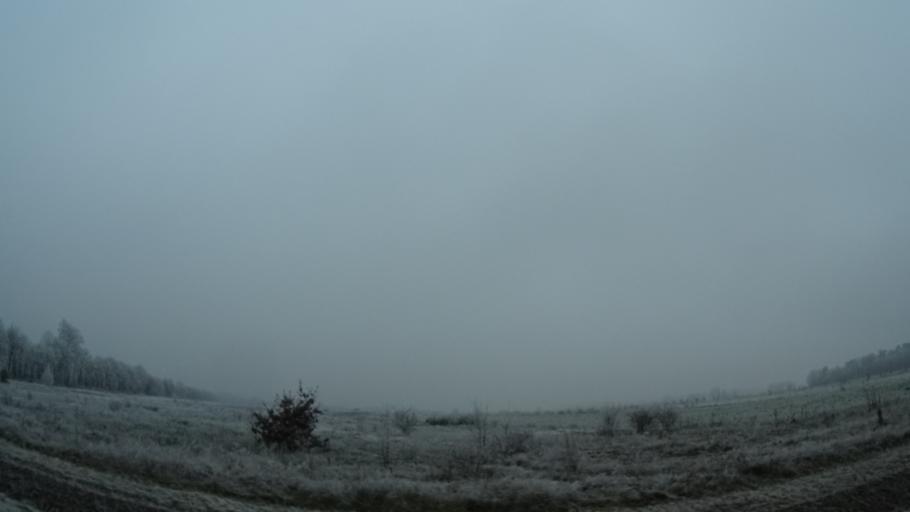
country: DE
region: Bavaria
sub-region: Regierungsbezirk Unterfranken
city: Albertshofen
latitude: 49.7625
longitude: 10.1880
